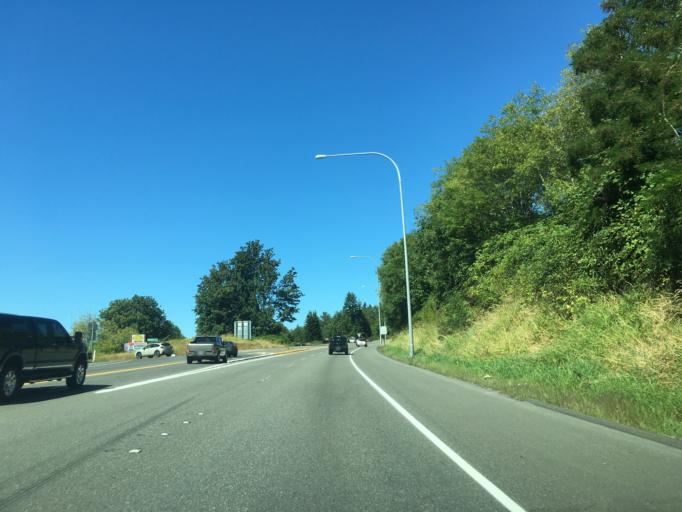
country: US
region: Washington
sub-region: Snohomish County
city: West Lake Stevens
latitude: 47.9822
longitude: -122.1374
